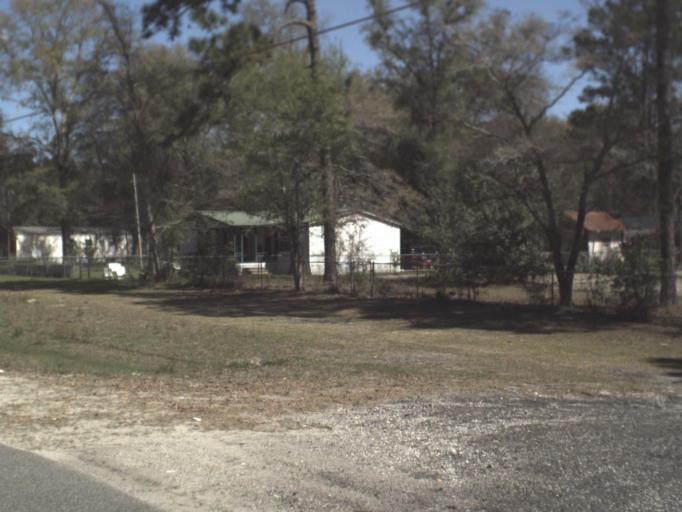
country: US
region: Florida
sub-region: Leon County
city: Woodville
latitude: 30.3278
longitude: -84.3114
